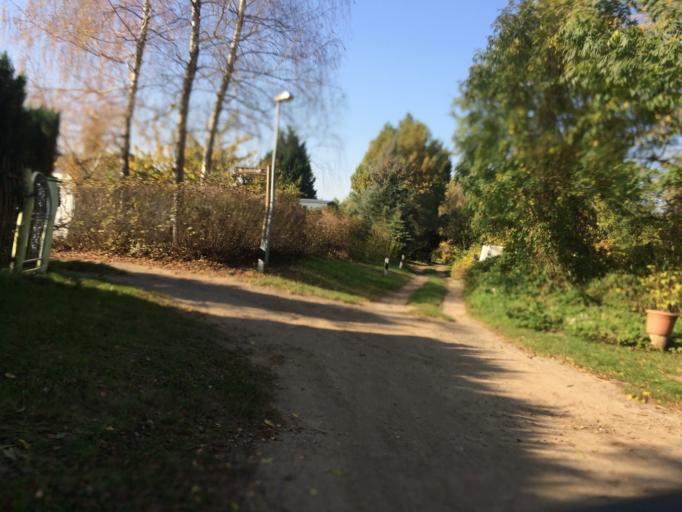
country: DE
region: Berlin
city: Blankenfelde
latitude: 52.6423
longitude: 13.4012
